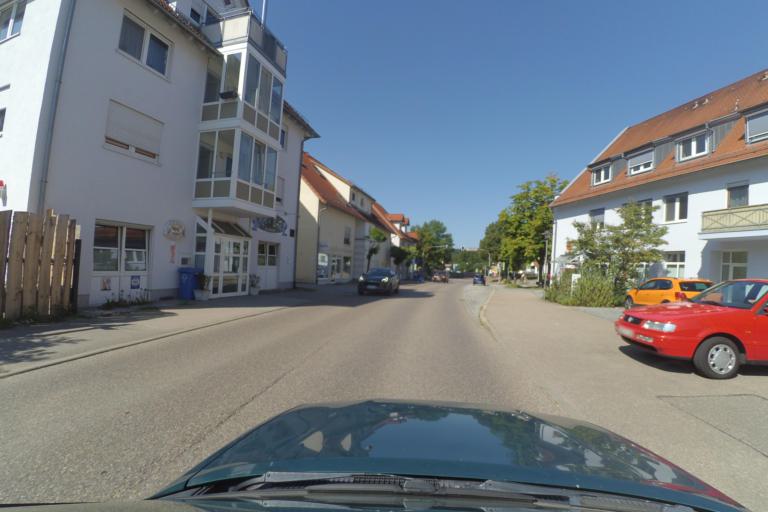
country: DE
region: Baden-Wuerttemberg
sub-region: Regierungsbezirk Stuttgart
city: Bobingen an der Rems
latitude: 48.8187
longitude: 9.9209
